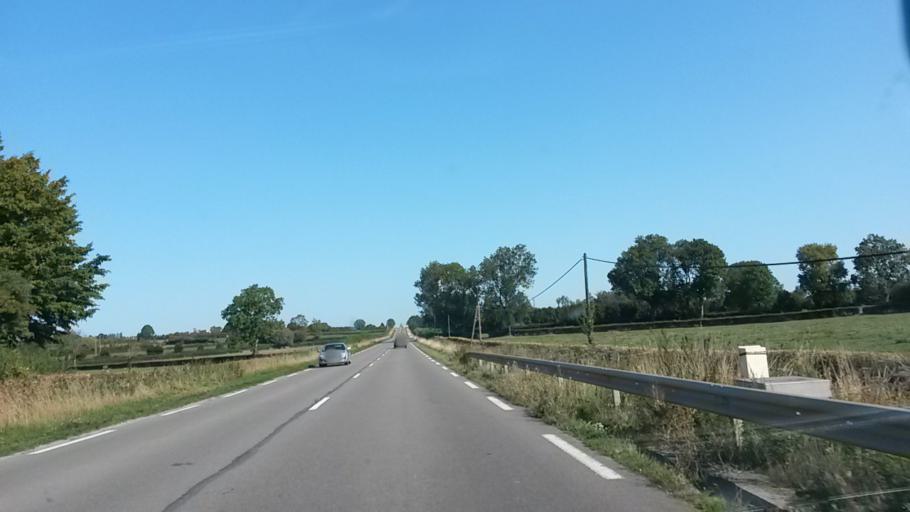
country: FR
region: Nord-Pas-de-Calais
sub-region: Departement du Nord
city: Avesnes-sur-Helpe
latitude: 50.0977
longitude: 3.9308
